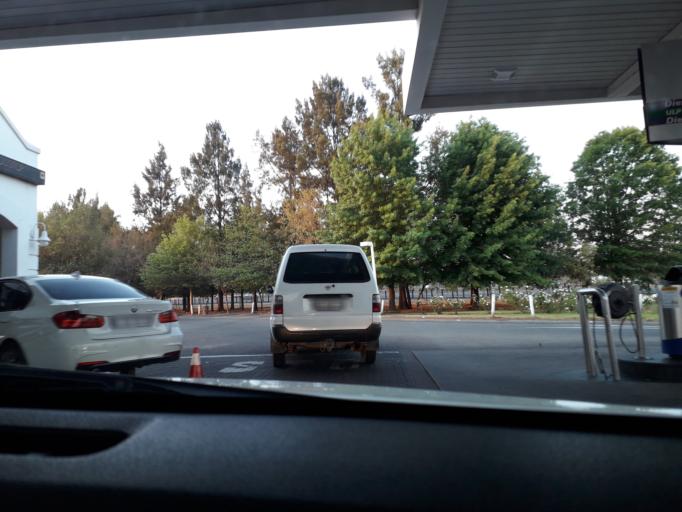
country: ZA
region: Gauteng
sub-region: Ekurhuleni Metropolitan Municipality
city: Tembisa
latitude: -26.0056
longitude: 28.2534
